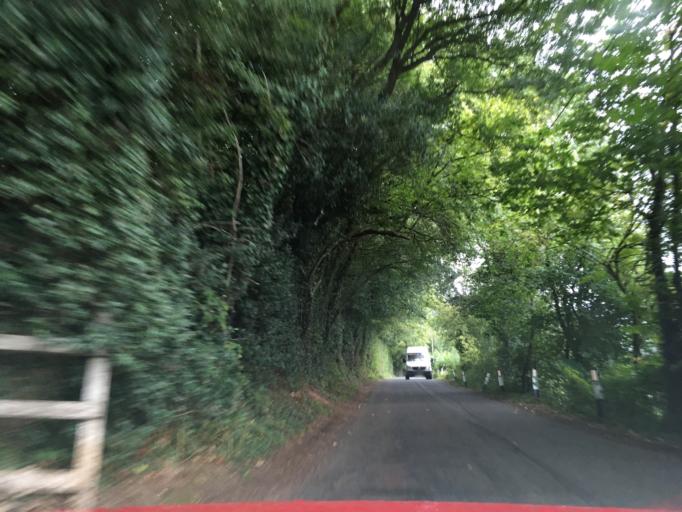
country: GB
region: Wales
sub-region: Monmouthshire
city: Llangybi
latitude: 51.6465
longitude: -2.8822
